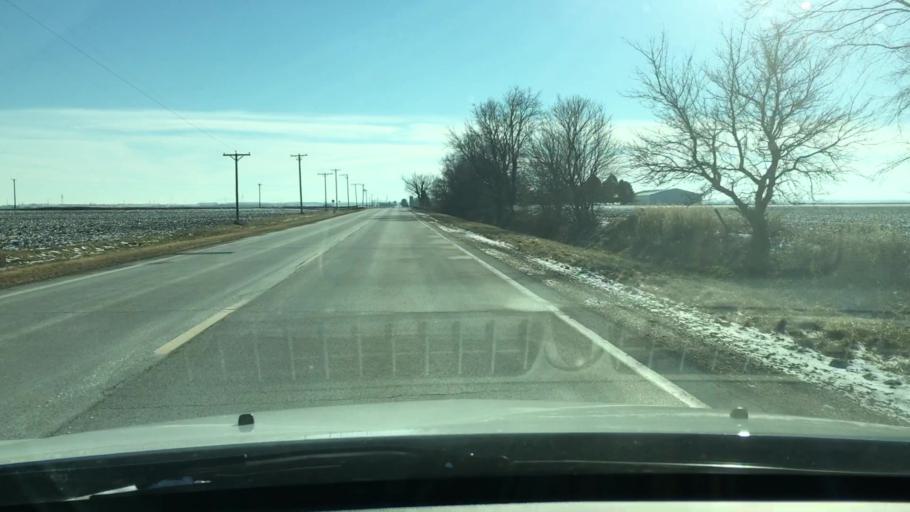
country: US
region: Illinois
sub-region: Ogle County
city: Rochelle
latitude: 41.8199
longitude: -89.0833
